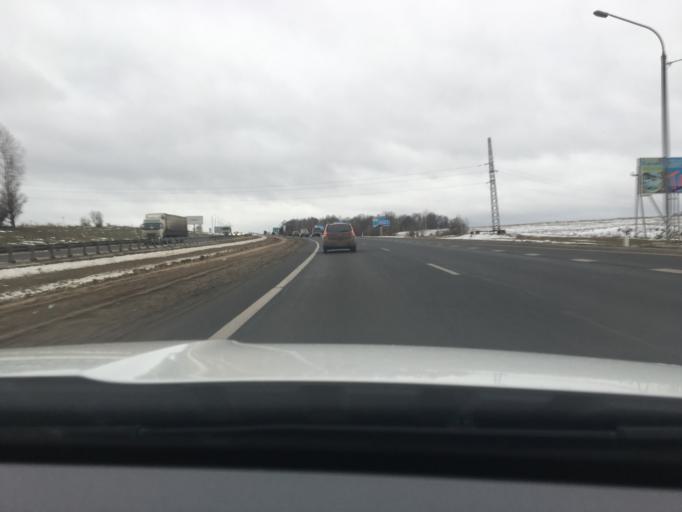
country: RU
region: Moskovskaya
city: Serpukhov
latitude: 54.8514
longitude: 37.4691
